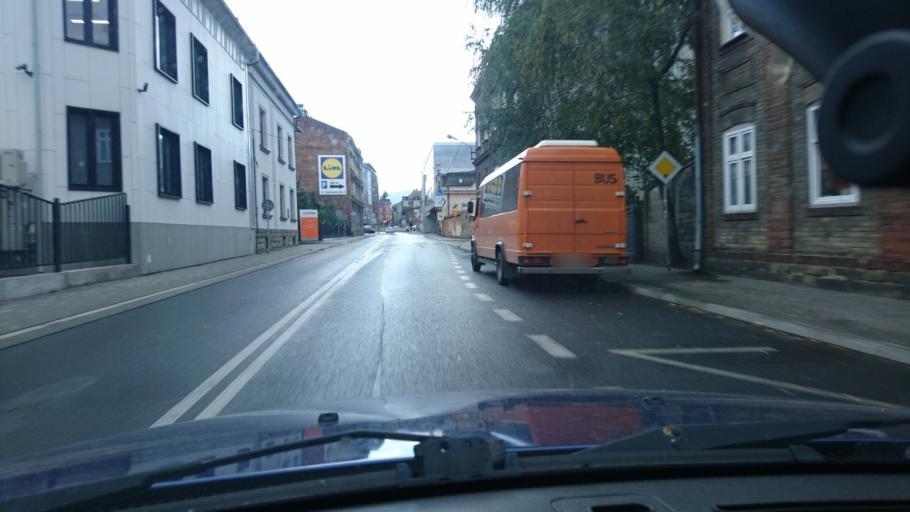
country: PL
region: Silesian Voivodeship
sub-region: Bielsko-Biala
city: Bielsko-Biala
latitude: 49.8279
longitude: 19.0479
